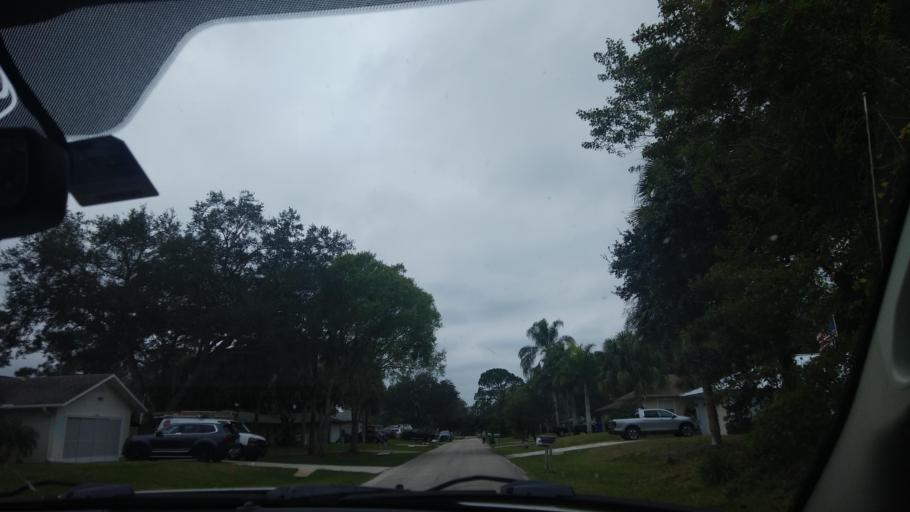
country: US
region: Florida
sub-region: Indian River County
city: Sebastian
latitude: 27.7708
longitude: -80.4879
